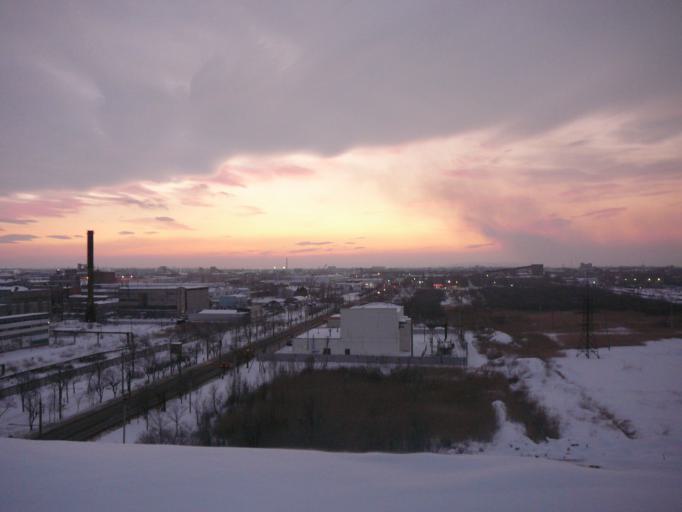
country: RU
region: Saratov
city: Engel's
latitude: 51.4668
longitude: 46.1502
